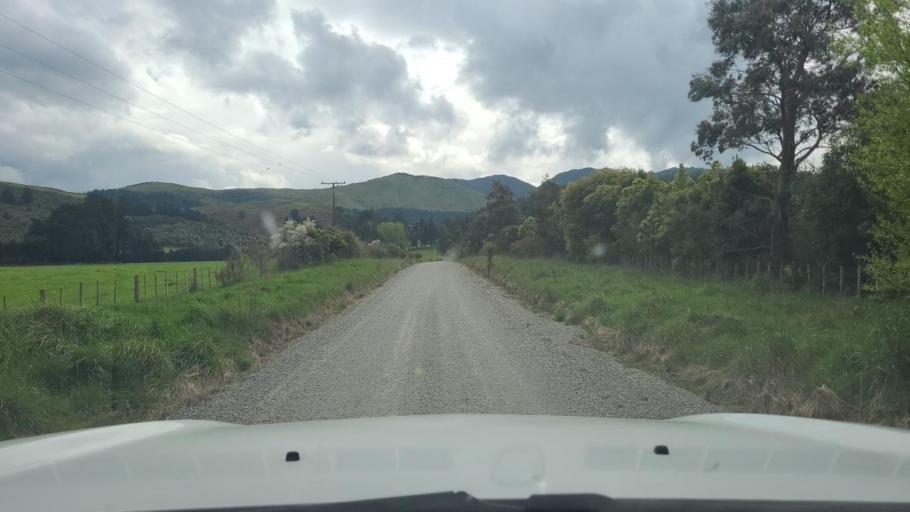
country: NZ
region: Wellington
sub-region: Masterton District
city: Masterton
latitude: -40.9956
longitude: 175.4889
